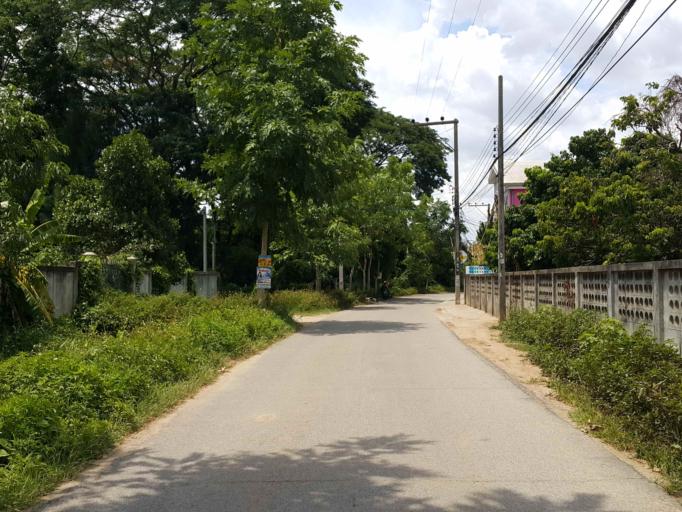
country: TH
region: Chiang Mai
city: Chiang Mai
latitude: 18.7463
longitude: 98.9884
